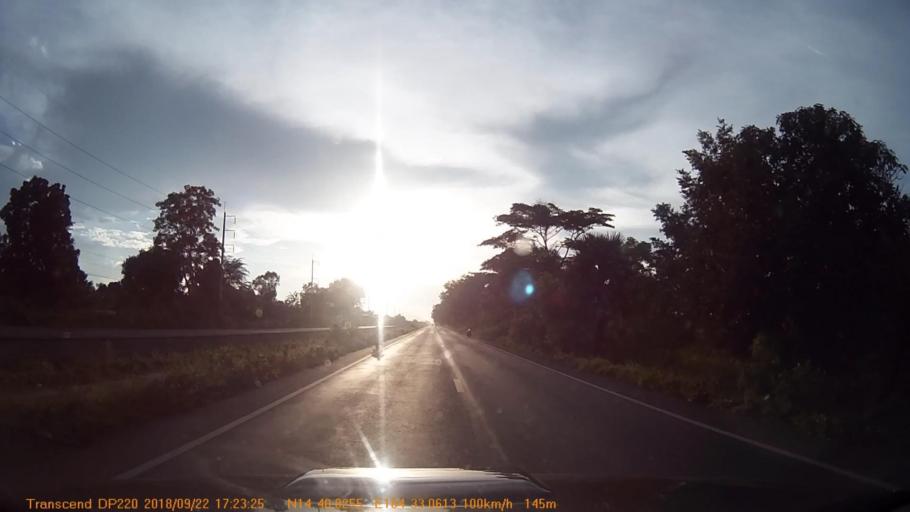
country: TH
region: Sisaket
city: Kantharalak
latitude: 14.6805
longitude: 104.5505
